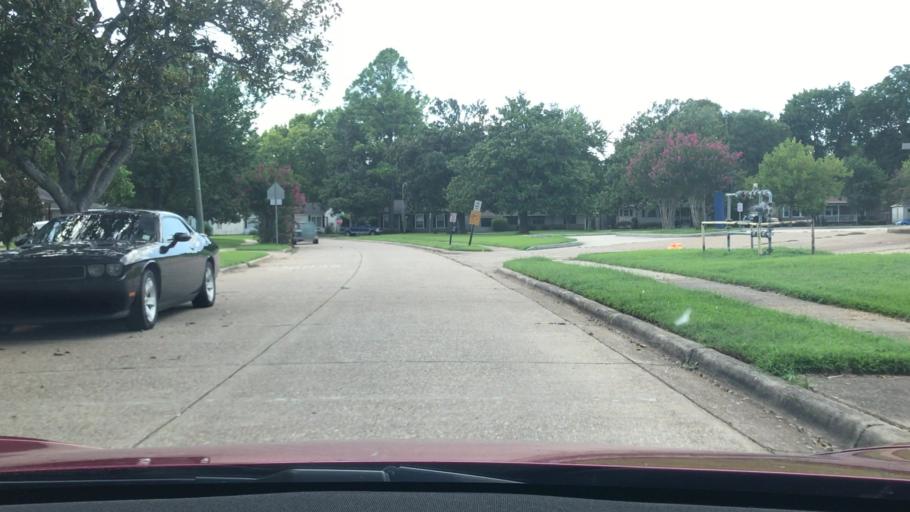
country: US
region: Louisiana
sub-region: Bossier Parish
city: Bossier City
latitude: 32.4590
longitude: -93.7184
